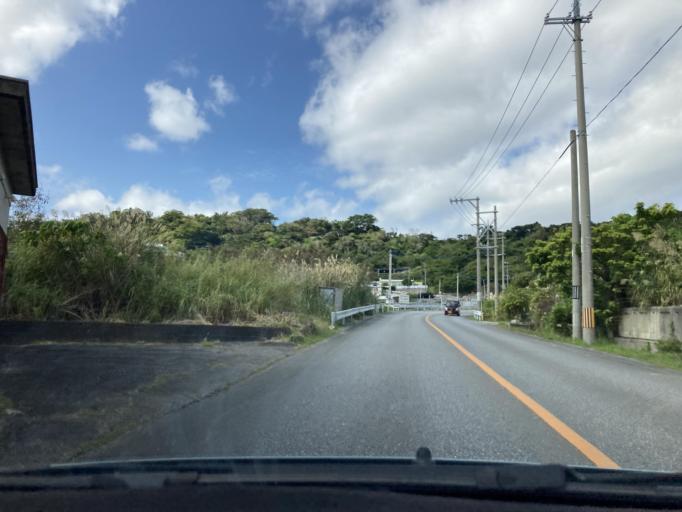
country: JP
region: Okinawa
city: Ginowan
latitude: 26.1827
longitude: 127.7632
